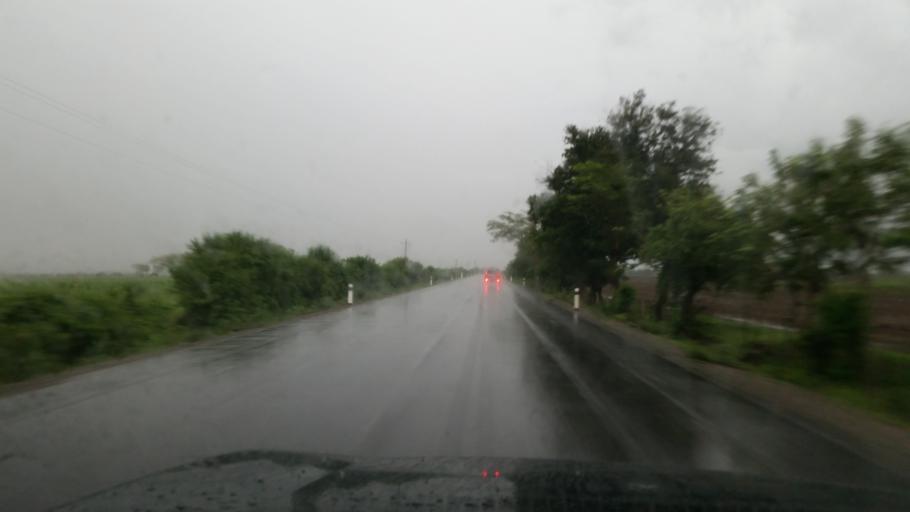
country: NI
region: Chinandega
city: Chichigalpa
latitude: 12.7812
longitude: -86.9318
